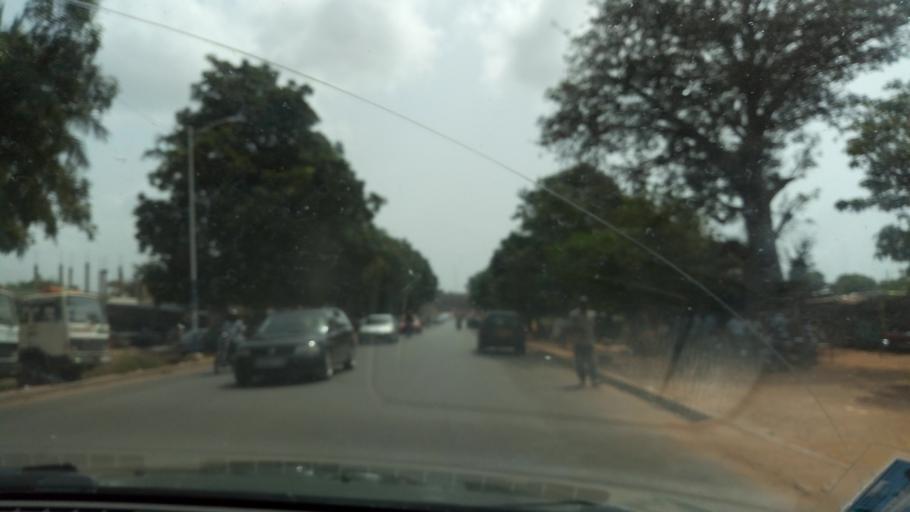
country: TG
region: Maritime
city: Lome
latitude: 6.1699
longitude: 1.1963
